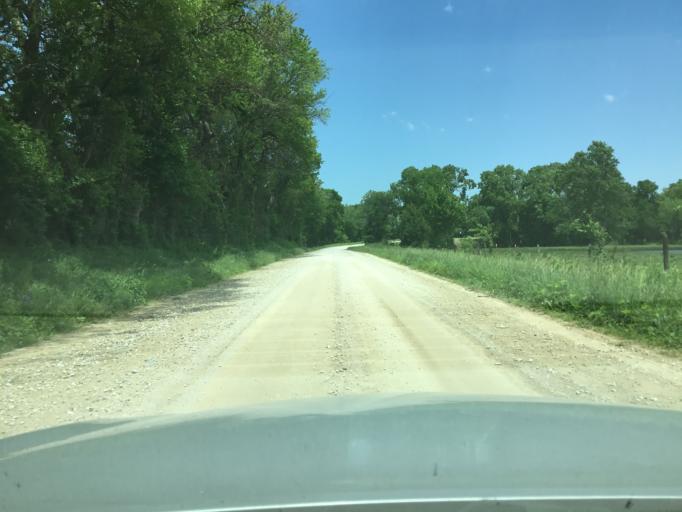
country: US
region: Kansas
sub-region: Montgomery County
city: Independence
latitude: 37.1068
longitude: -95.7830
